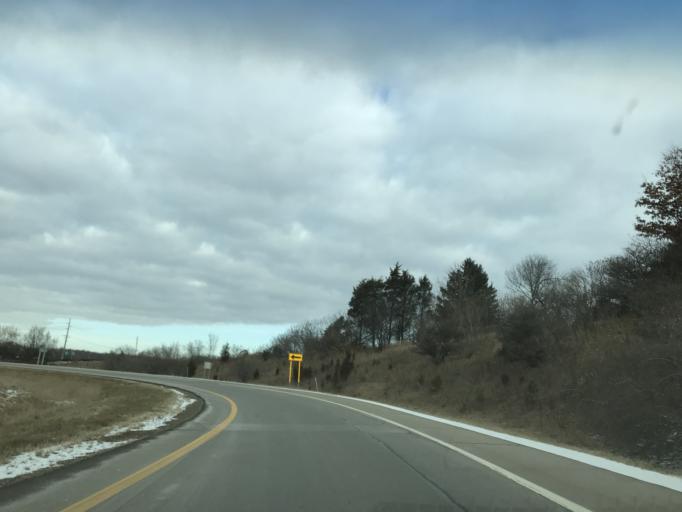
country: US
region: Michigan
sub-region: Oakland County
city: Clarkston
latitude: 42.7365
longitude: -83.3775
